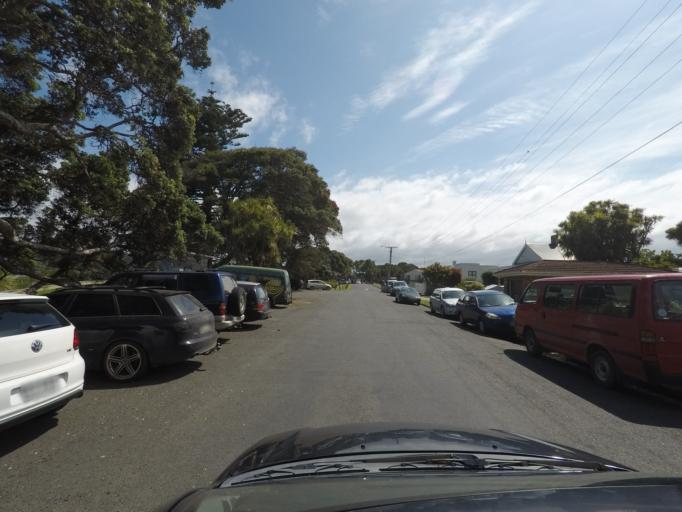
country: NZ
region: Waikato
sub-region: Waikato District
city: Raglan
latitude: -37.7991
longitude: 174.8674
